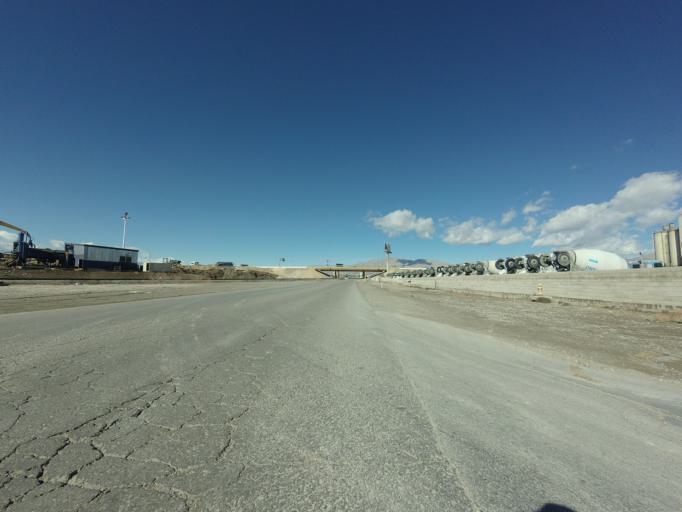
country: US
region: Nevada
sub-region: Clark County
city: Nellis Air Force Base
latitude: 36.2677
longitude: -115.0588
